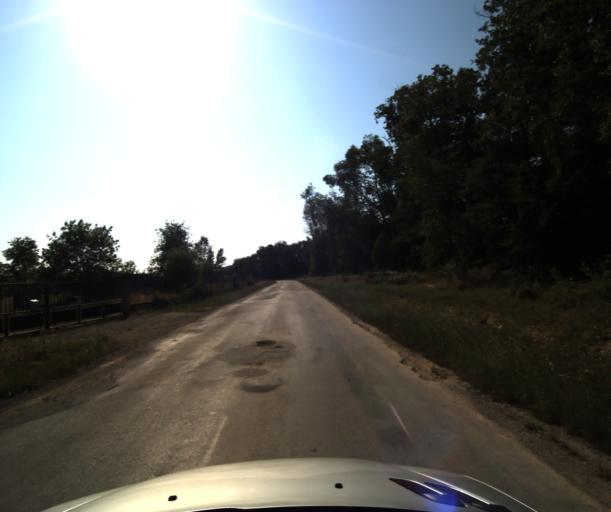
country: FR
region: Midi-Pyrenees
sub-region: Departement de la Haute-Garonne
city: Lacroix-Falgarde
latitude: 43.4770
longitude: 1.4048
